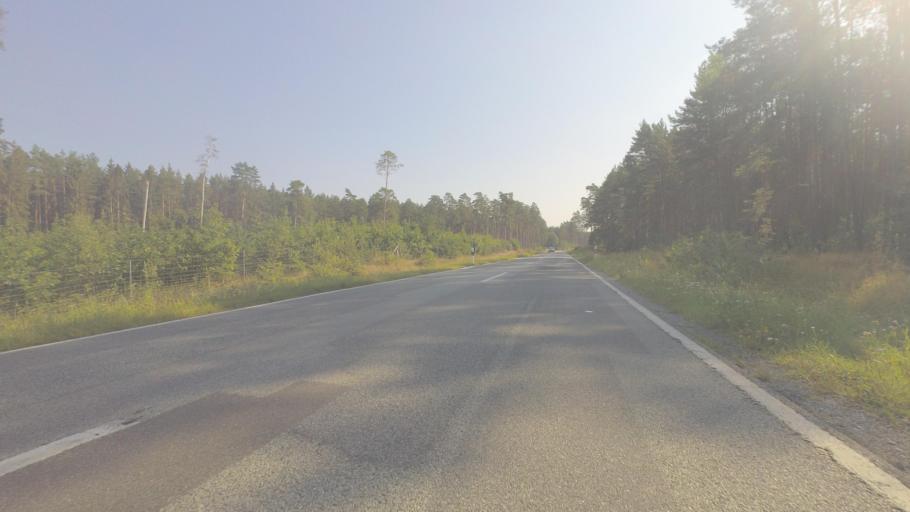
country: DE
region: Mecklenburg-Vorpommern
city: Malchow
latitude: 53.5475
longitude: 12.4407
